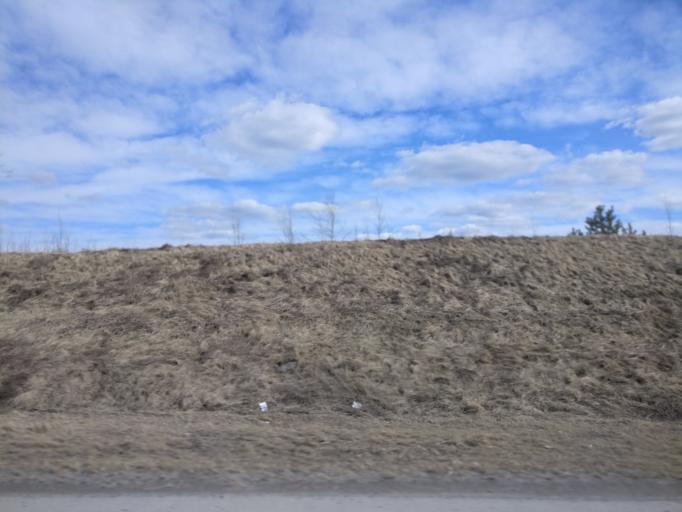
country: FI
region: Pirkanmaa
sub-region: Tampere
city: Lempaeaelae
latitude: 61.3539
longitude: 23.7910
